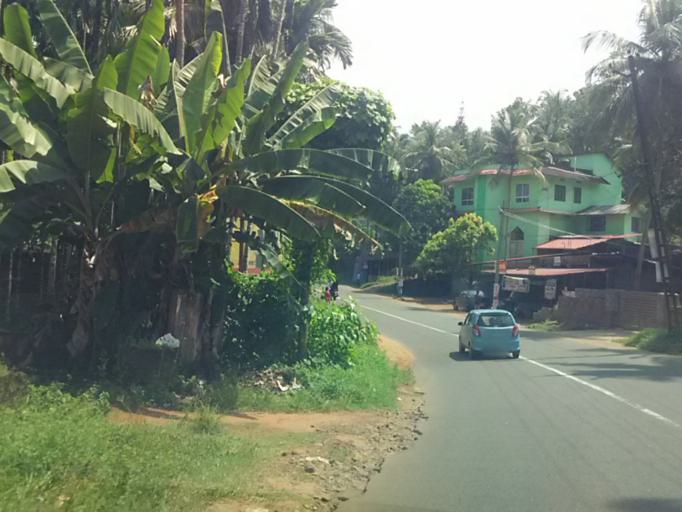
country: IN
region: Kerala
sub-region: Kozhikode
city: Kunnamangalam
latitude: 11.3294
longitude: 75.8885
